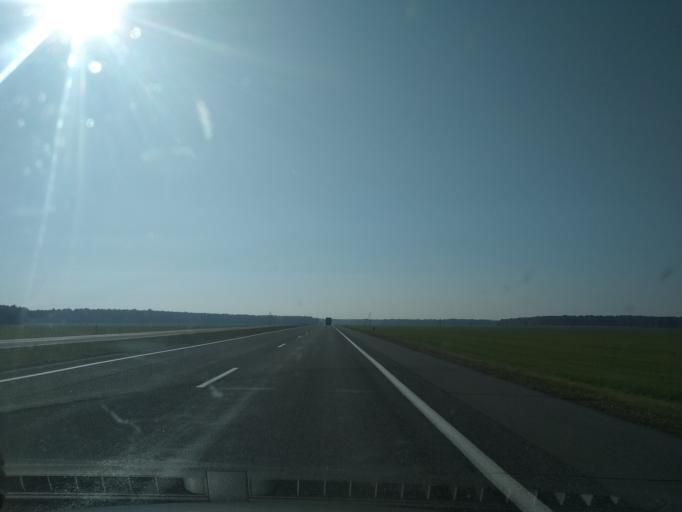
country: BY
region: Brest
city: Antopal'
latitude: 52.3001
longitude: 24.5864
